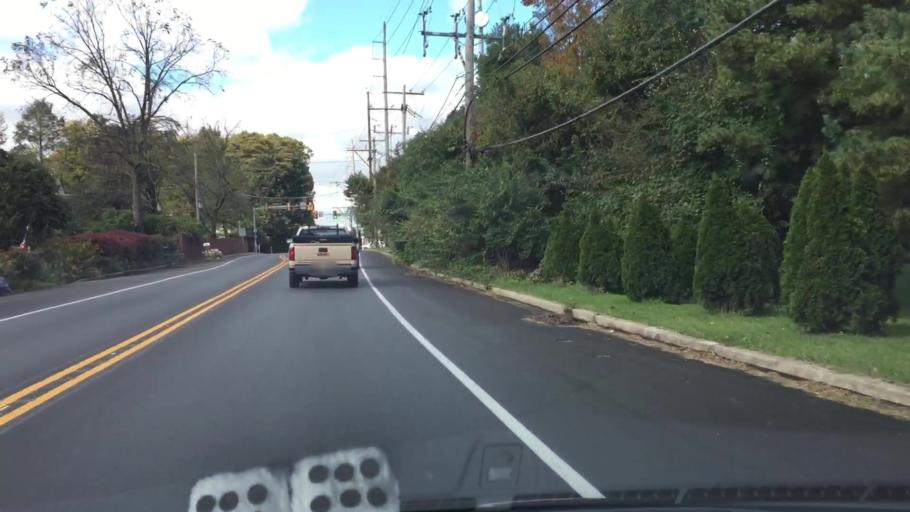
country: US
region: Pennsylvania
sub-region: Chester County
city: Malvern
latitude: 39.9752
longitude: -75.5349
